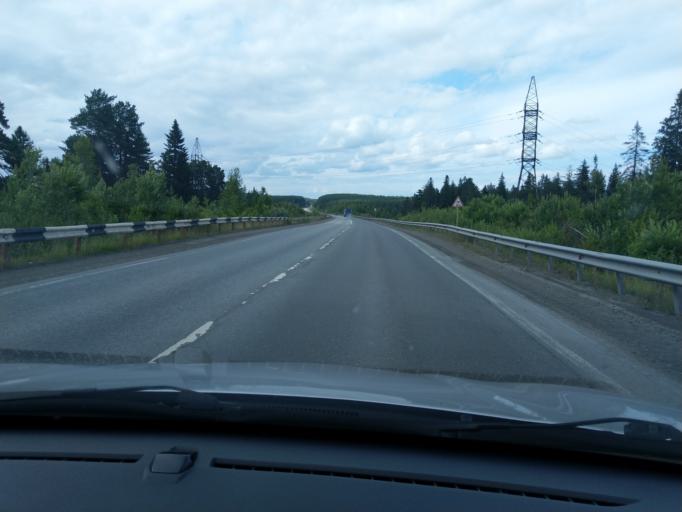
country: RU
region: Sverdlovsk
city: Nizhniy Tagil
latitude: 57.9345
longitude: 59.8665
